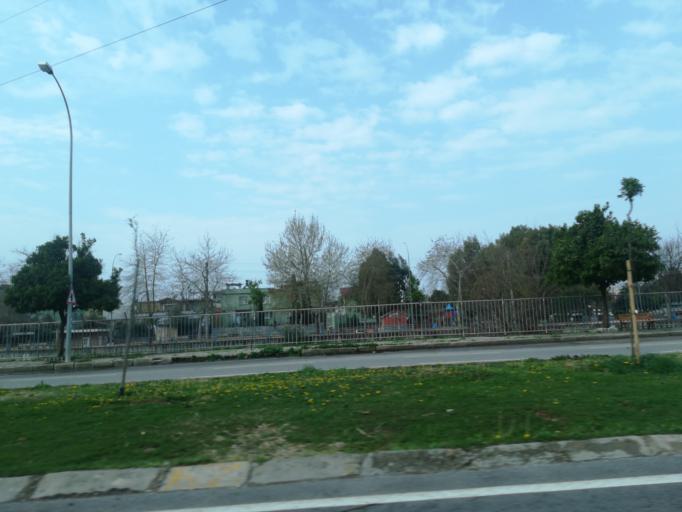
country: TR
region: Adana
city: Yuregir
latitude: 36.9925
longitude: 35.3617
